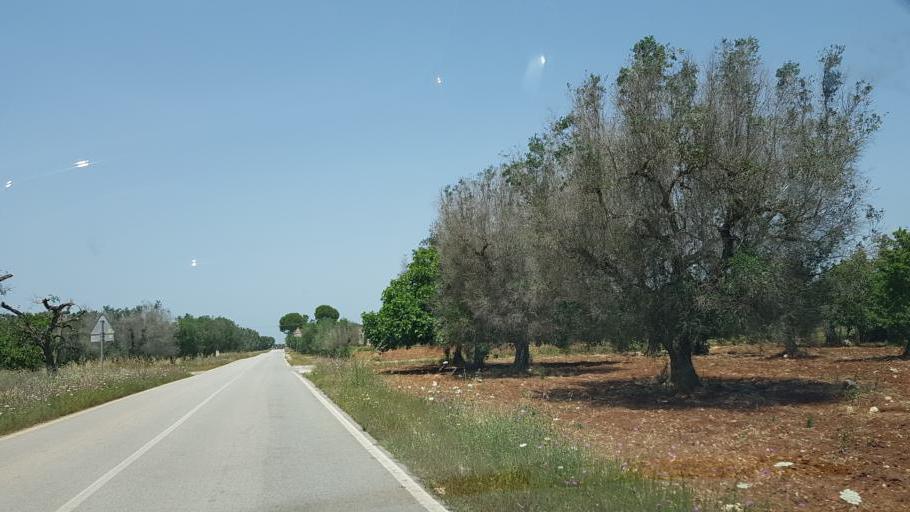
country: IT
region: Apulia
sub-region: Provincia di Brindisi
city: San Pancrazio Salentino
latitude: 40.4552
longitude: 17.8401
